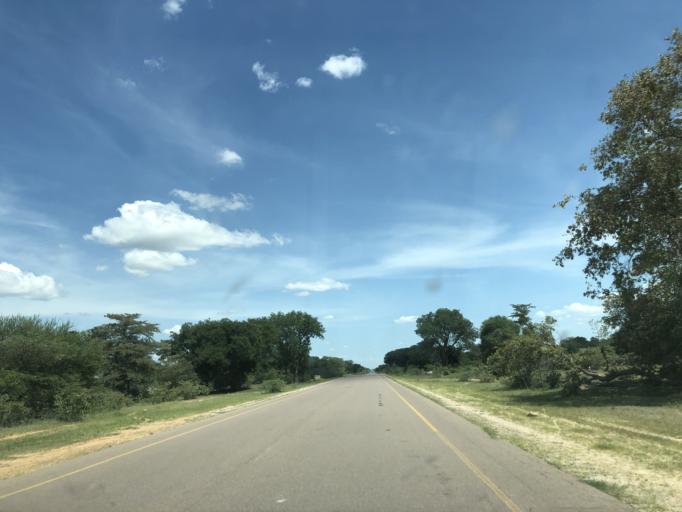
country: AO
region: Cunene
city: Ondjiva
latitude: -16.8533
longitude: 15.4685
